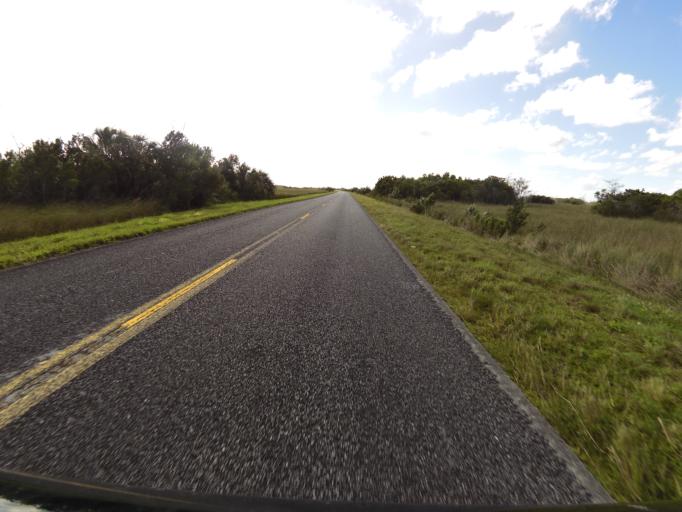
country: US
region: Florida
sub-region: Miami-Dade County
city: Florida City
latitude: 25.3885
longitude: -80.8048
